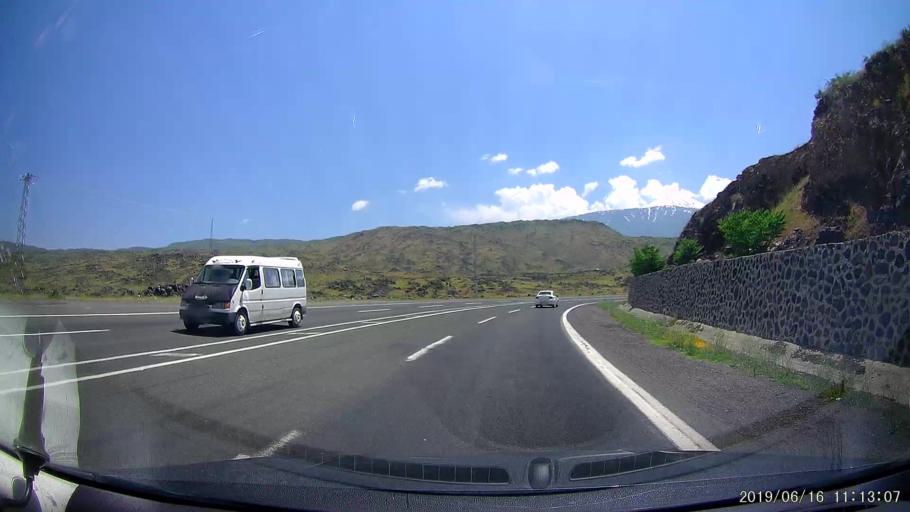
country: TR
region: Igdir
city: Igdir
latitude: 39.7878
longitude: 44.1337
